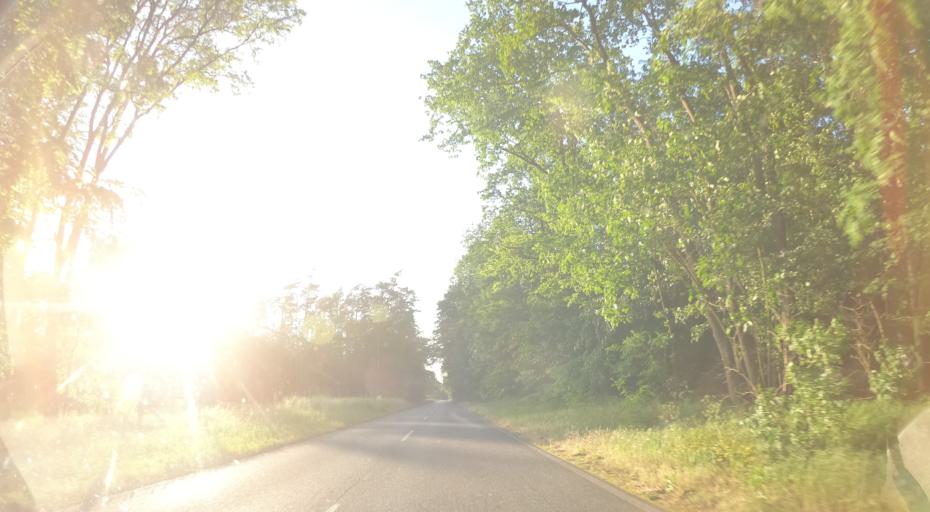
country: PL
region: West Pomeranian Voivodeship
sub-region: Powiat mysliborski
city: Nowogrodek Pomorski
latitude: 52.8539
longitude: 15.0357
